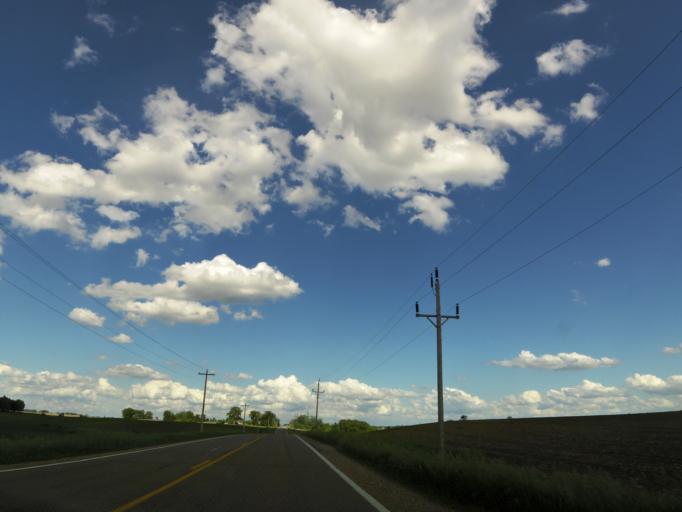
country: US
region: Minnesota
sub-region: Wright County
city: Cokato
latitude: 45.0661
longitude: -94.2260
